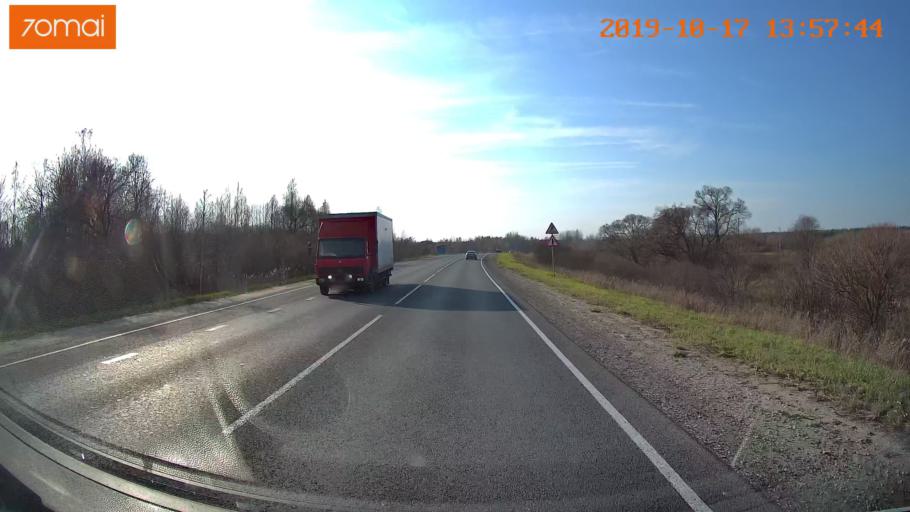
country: RU
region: Rjazan
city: Spas-Klepiki
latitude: 55.1417
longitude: 40.2407
